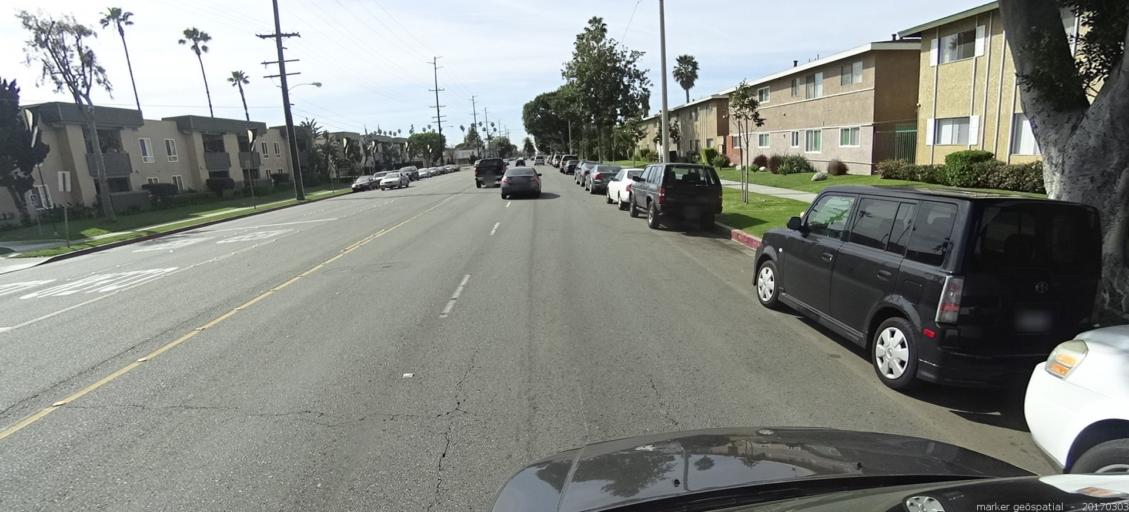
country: US
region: California
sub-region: Orange County
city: Anaheim
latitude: 33.8180
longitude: -117.9346
